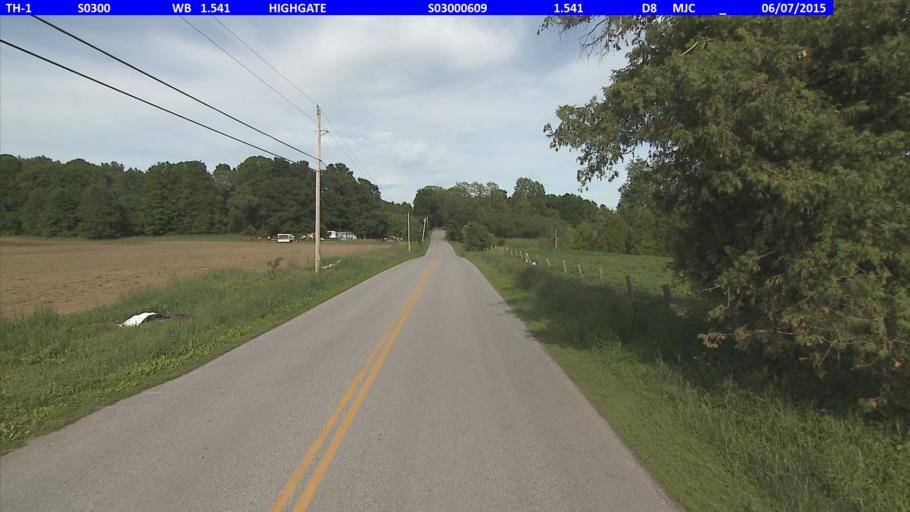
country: US
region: Vermont
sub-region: Franklin County
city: Swanton
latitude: 44.9487
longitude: -73.0859
